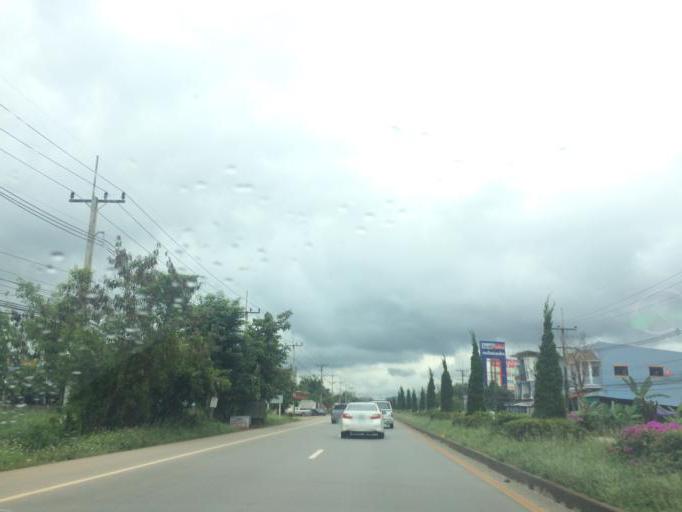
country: TH
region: Chiang Rai
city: Chiang Rai
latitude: 20.0195
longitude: 99.8706
